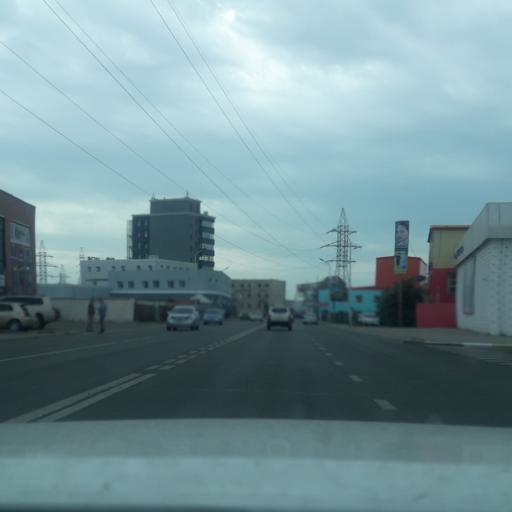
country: MN
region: Ulaanbaatar
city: Ulaanbaatar
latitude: 47.9018
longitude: 106.8685
